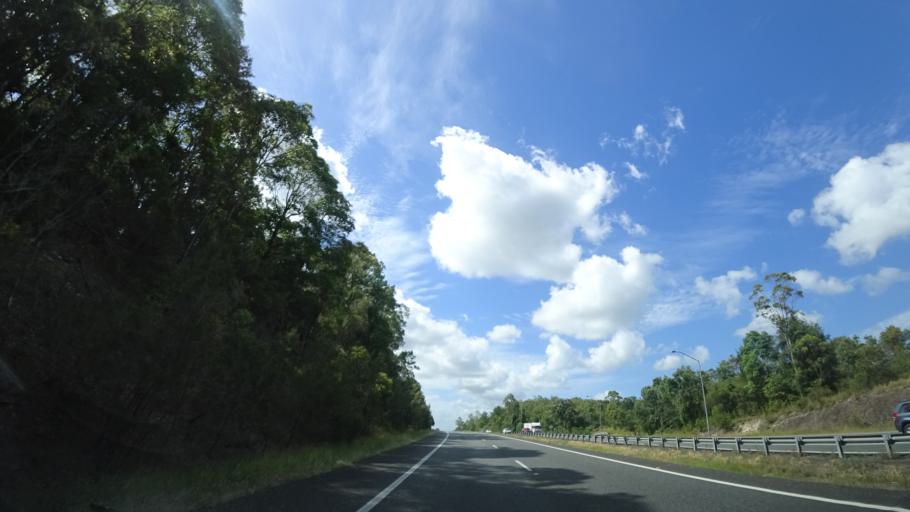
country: AU
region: Queensland
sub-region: Sunshine Coast
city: Twin Waters
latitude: -26.5957
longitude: 152.9714
